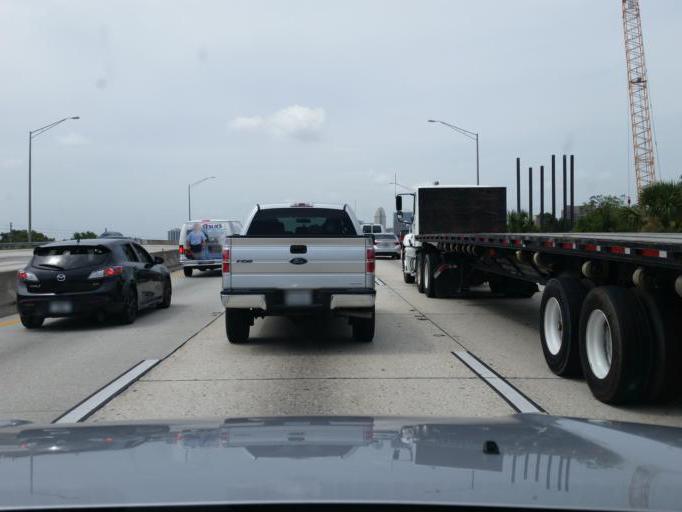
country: US
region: Florida
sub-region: Orange County
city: Fairview Shores
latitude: 28.5688
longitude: -81.3758
